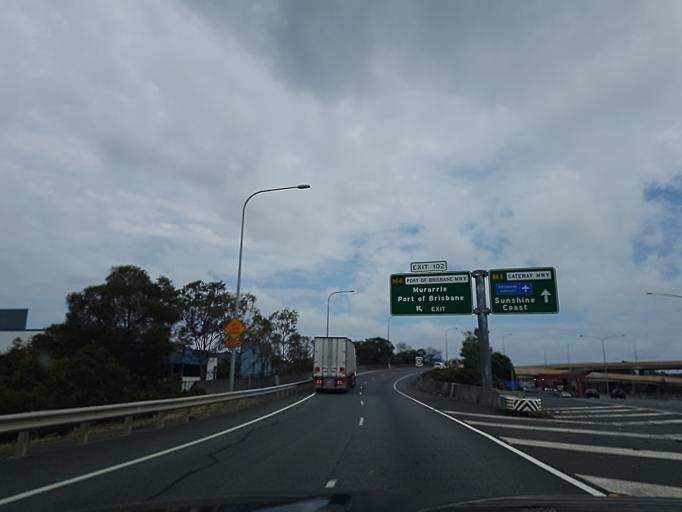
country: AU
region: Queensland
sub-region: Brisbane
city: Cannon Hill
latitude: -27.4603
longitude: 153.1096
